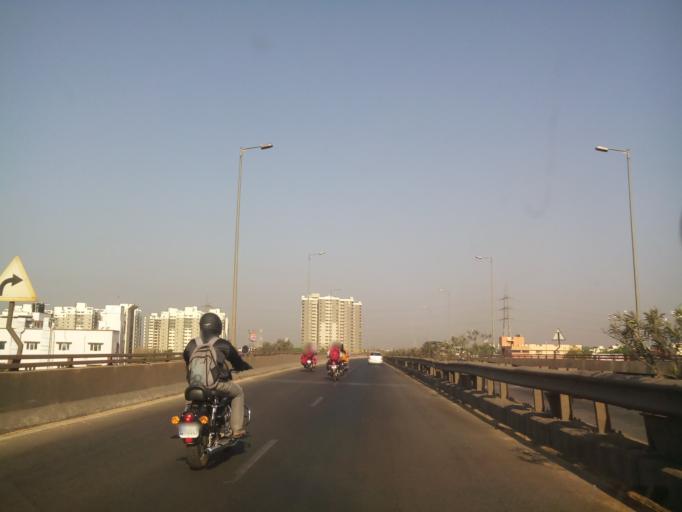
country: IN
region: Karnataka
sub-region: Bangalore Urban
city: Yelahanka
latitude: 13.0455
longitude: 77.5068
